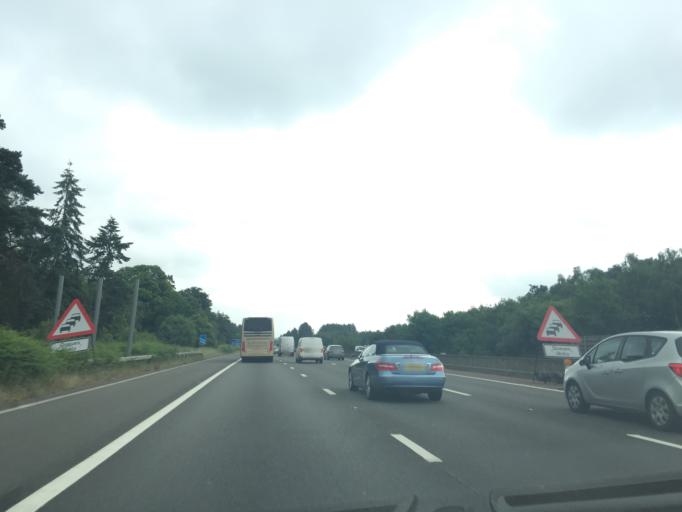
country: GB
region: England
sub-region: Hampshire
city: Fleet
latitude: 51.2947
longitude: -0.8651
